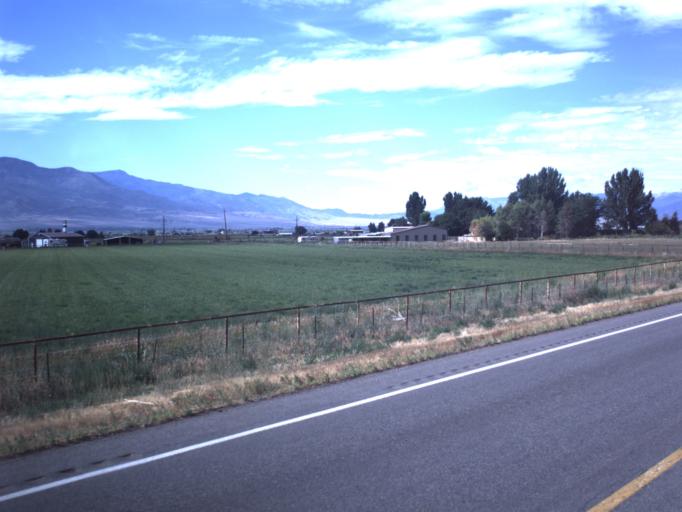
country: US
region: Utah
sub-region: Sevier County
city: Richfield
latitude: 38.7848
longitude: -112.0555
